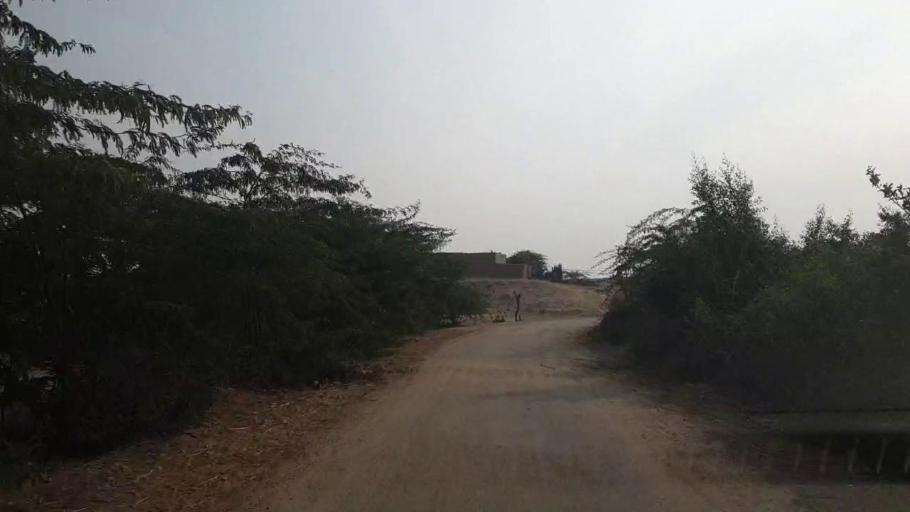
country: PK
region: Sindh
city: Sann
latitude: 26.0570
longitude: 68.1020
